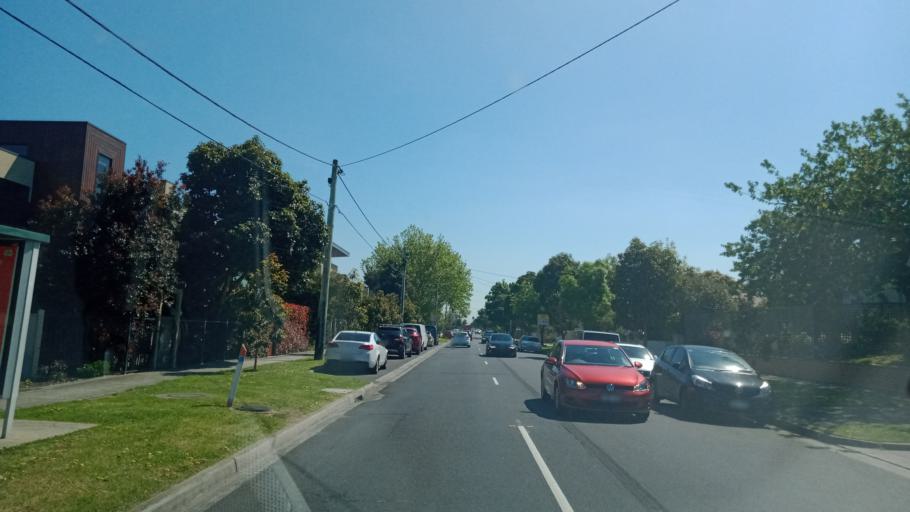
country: AU
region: Victoria
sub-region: Monash
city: Oakleigh South
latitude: -37.9222
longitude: 145.0734
